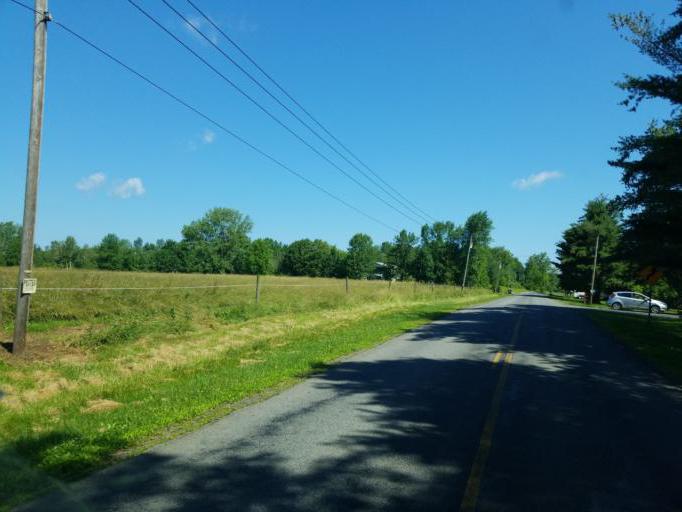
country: US
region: New York
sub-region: Wayne County
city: Wolcott
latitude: 43.2015
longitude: -76.8686
